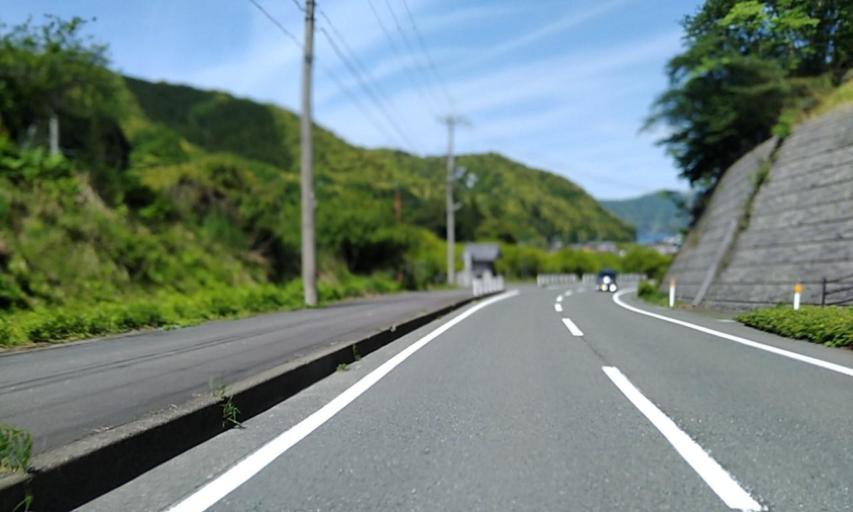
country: JP
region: Fukui
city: Obama
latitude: 35.5338
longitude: 135.7805
